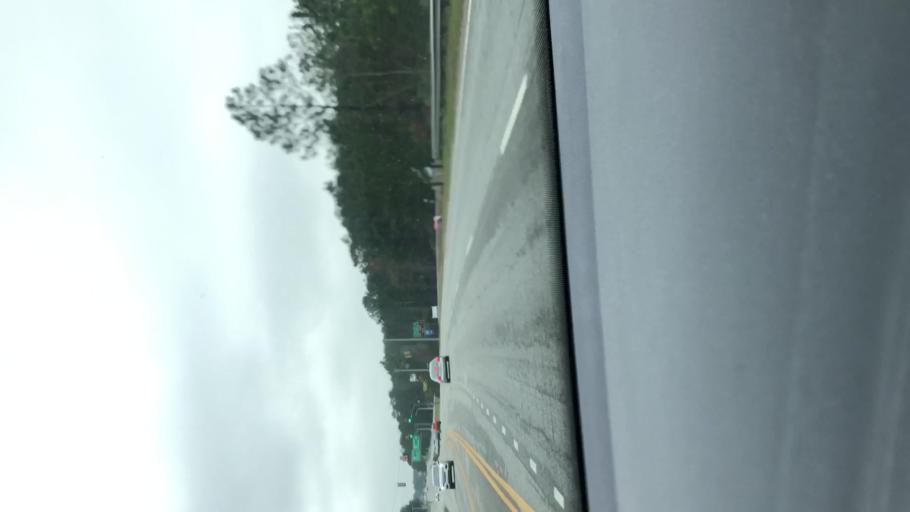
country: US
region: South Carolina
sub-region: Jasper County
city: Hardeeville
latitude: 32.3126
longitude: -81.0535
